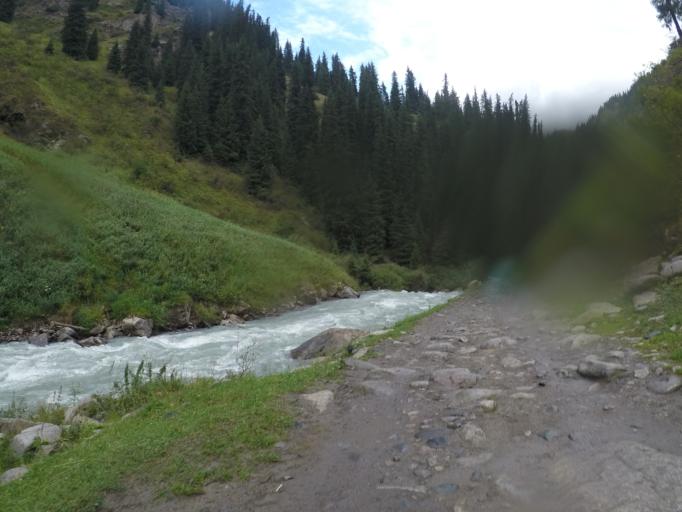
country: KG
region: Ysyk-Koel
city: Teploklyuchenka
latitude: 42.4152
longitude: 78.5712
